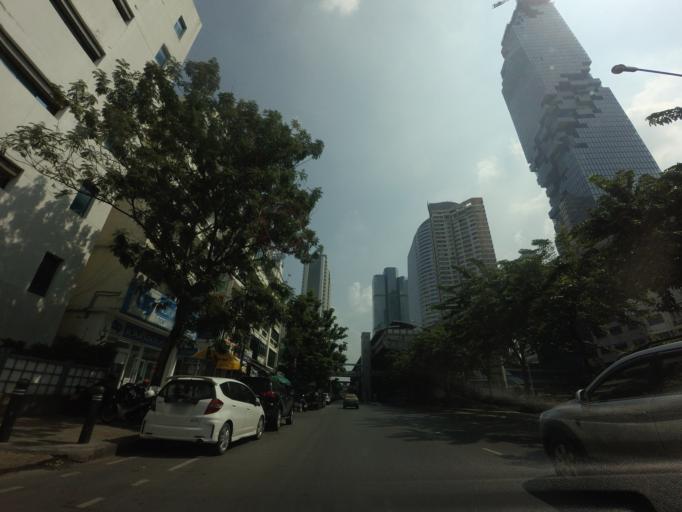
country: TH
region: Bangkok
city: Bang Rak
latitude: 13.7251
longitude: 100.5288
